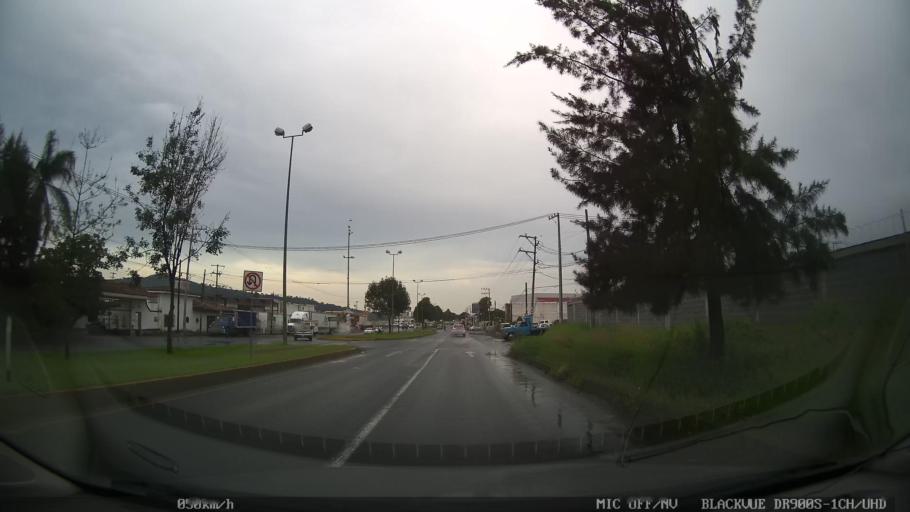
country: MX
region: Michoacan
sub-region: Uruapan
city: Santa Rosa (Santa Barbara)
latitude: 19.3825
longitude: -102.0450
